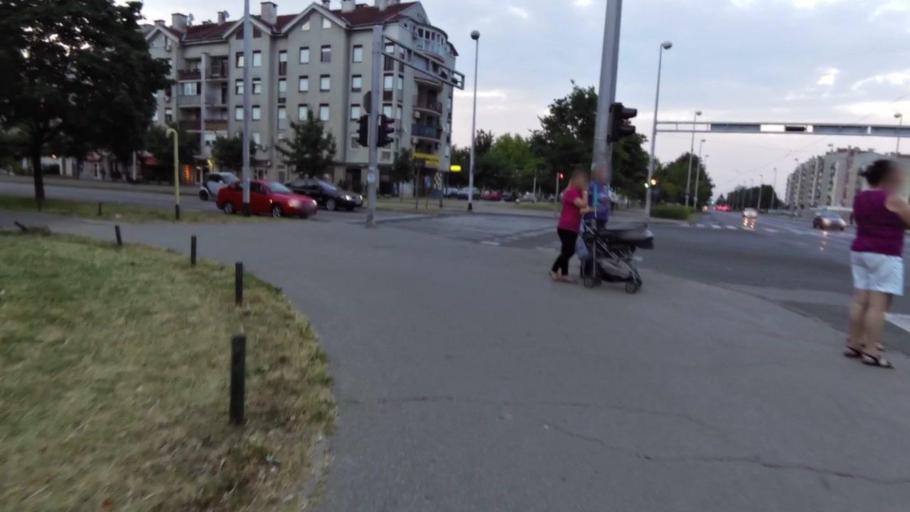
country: HR
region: Grad Zagreb
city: Dubrava
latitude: 45.8289
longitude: 16.0685
